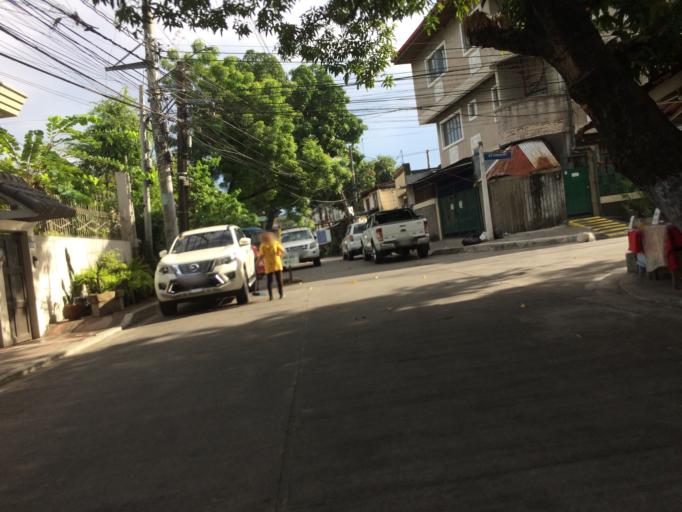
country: PH
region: Calabarzon
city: Bagong Pagasa
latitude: 14.6720
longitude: 121.0207
